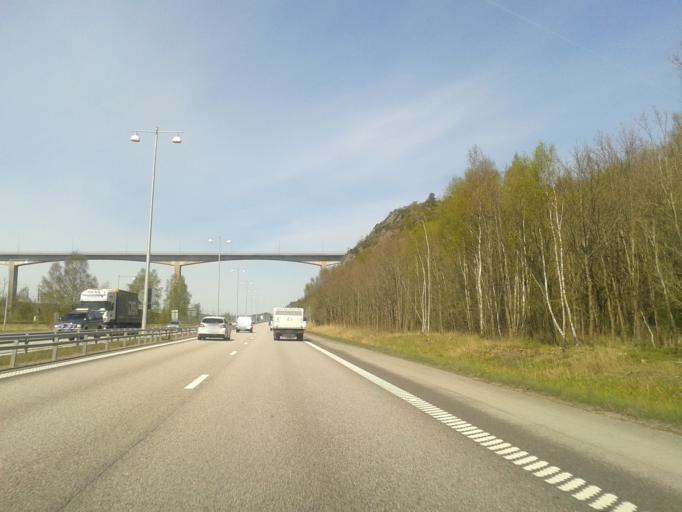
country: SE
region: Vaestra Goetaland
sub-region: Goteborg
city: Gardsten
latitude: 57.7944
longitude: 12.0158
